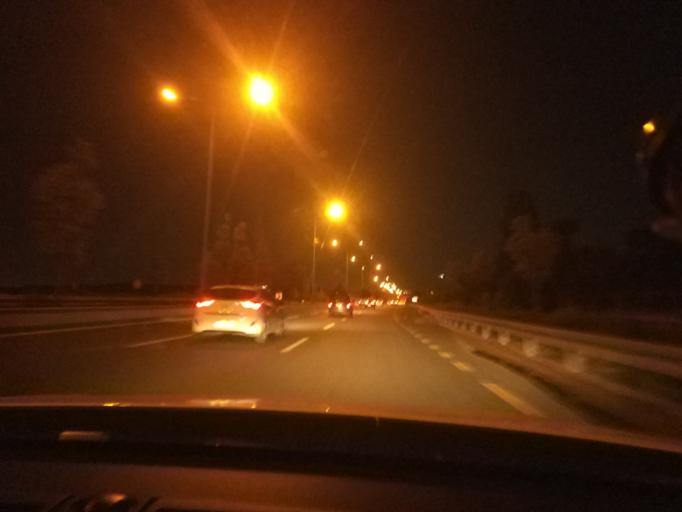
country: TR
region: Ankara
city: Batikent
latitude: 39.9150
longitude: 32.7543
